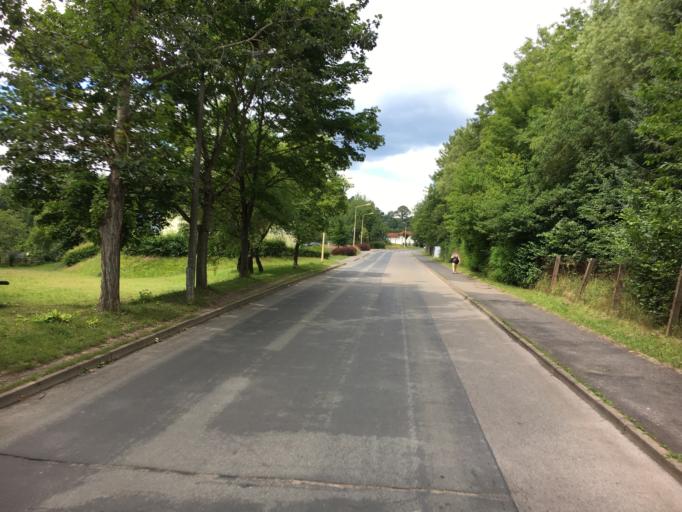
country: DE
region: Thuringia
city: Schmalkalden
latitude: 50.7211
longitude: 10.4700
